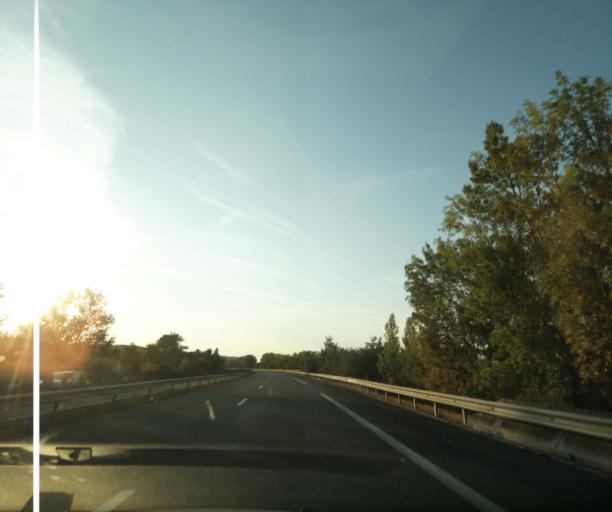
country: FR
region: Aquitaine
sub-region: Departement du Lot-et-Garonne
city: Layrac
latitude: 44.1412
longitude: 0.6659
